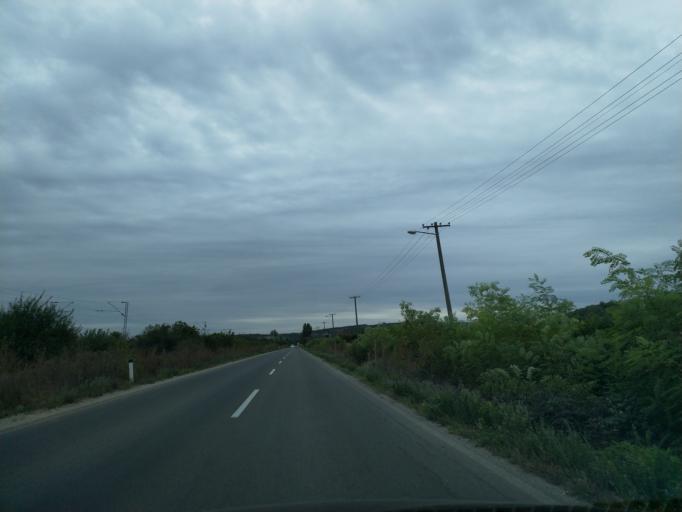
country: RS
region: Central Serbia
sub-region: Sumadijski Okrug
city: Batocina
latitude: 44.1278
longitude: 21.1312
